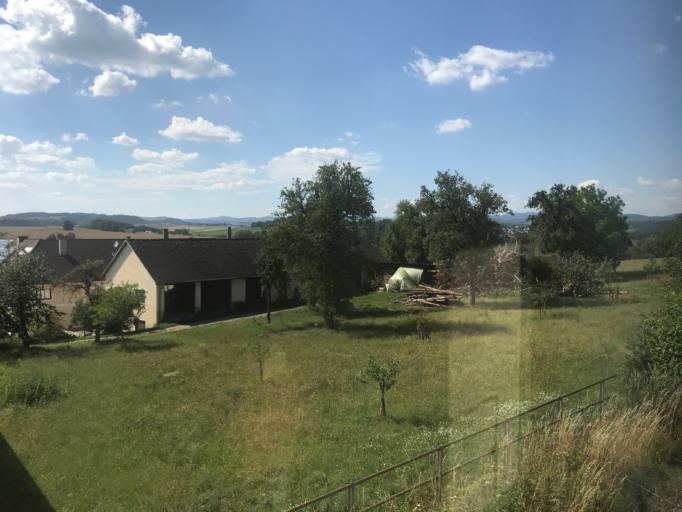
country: AT
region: Upper Austria
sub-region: Politischer Bezirk Urfahr-Umgebung
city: Engerwitzdorf
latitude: 48.2976
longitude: 14.4869
